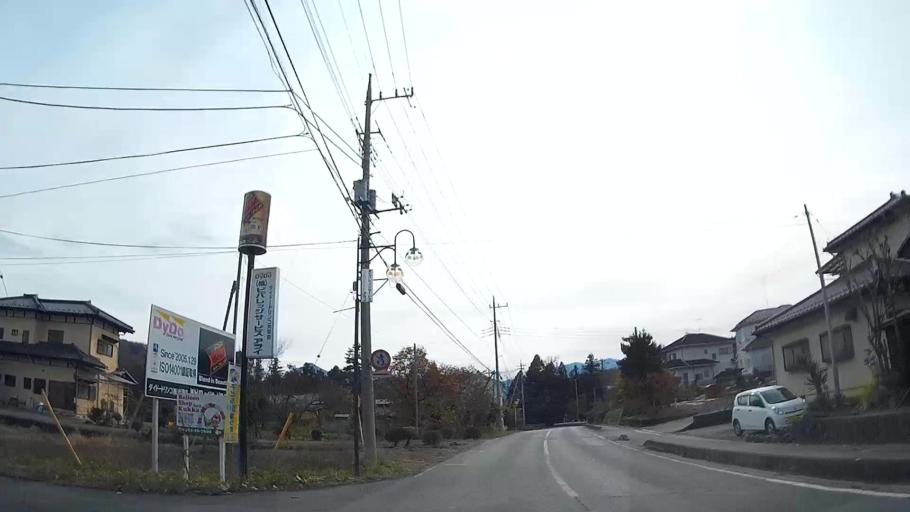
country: JP
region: Saitama
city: Chichibu
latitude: 36.0281
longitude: 139.0379
